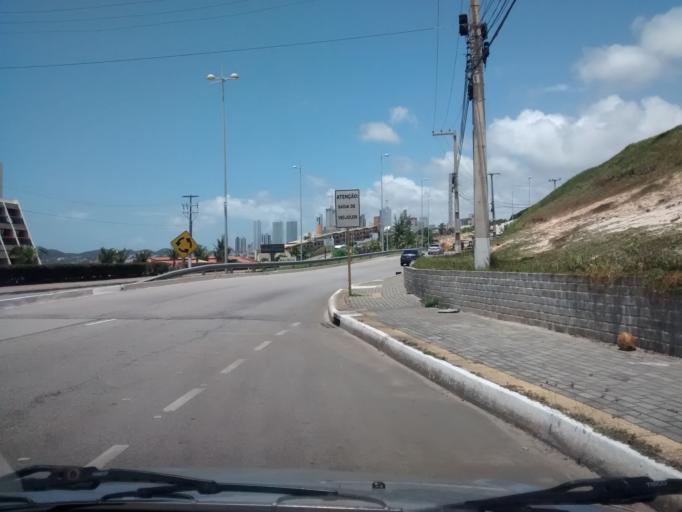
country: BR
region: Rio Grande do Norte
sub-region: Natal
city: Natal
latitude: -5.8623
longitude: -35.1811
